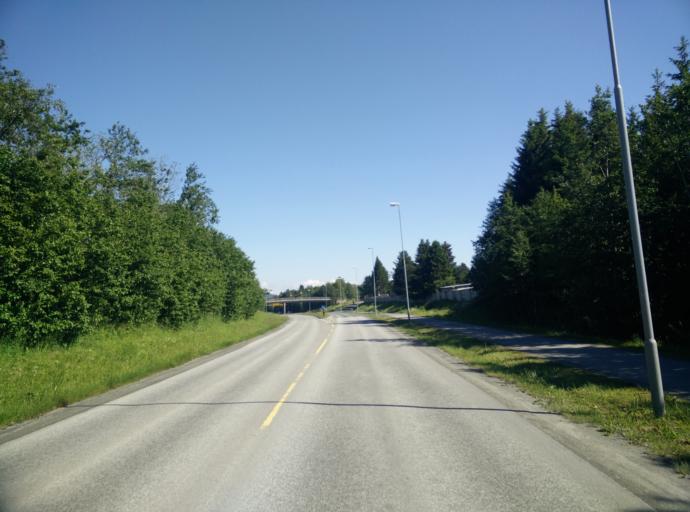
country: NO
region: Sor-Trondelag
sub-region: Trondheim
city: Trondheim
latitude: 63.3716
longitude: 10.3368
